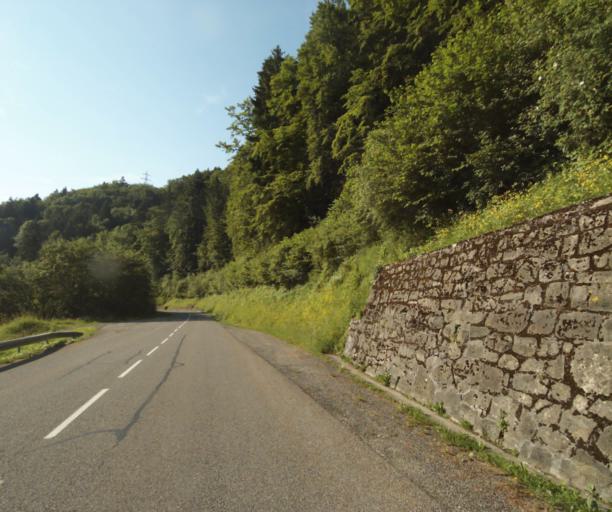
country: FR
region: Rhone-Alpes
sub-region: Departement de la Haute-Savoie
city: Lyaud
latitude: 46.3399
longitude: 6.5456
